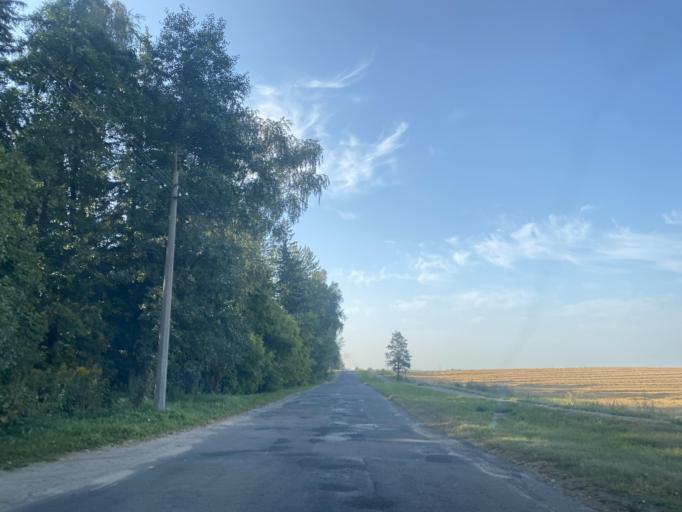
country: BY
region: Minsk
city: Hatava
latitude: 53.8312
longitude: 27.6386
